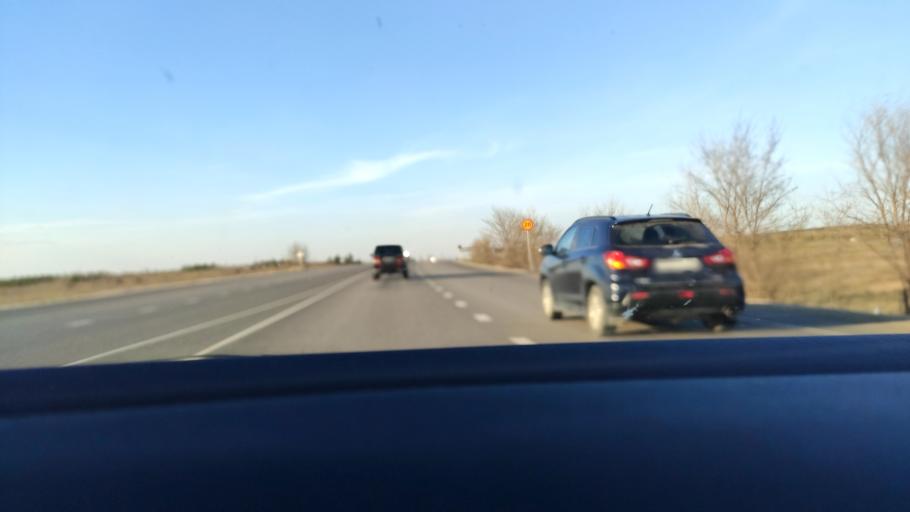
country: RU
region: Voronezj
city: Kolodeznyy
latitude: 51.3531
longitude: 39.1744
